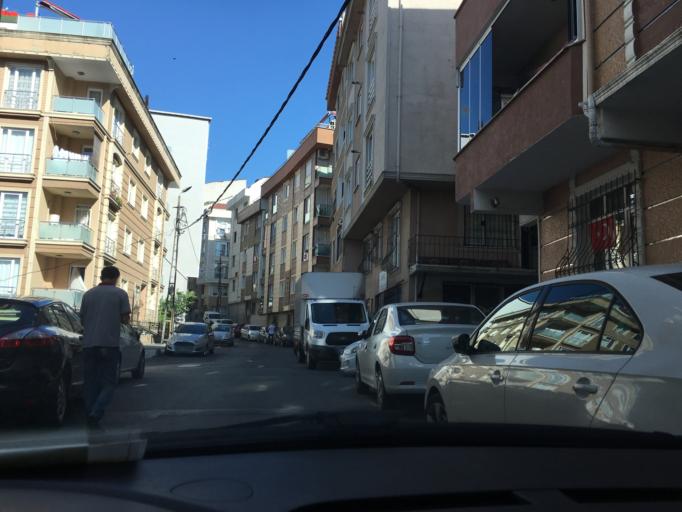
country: TR
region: Istanbul
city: Sisli
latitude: 41.0537
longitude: 28.9729
